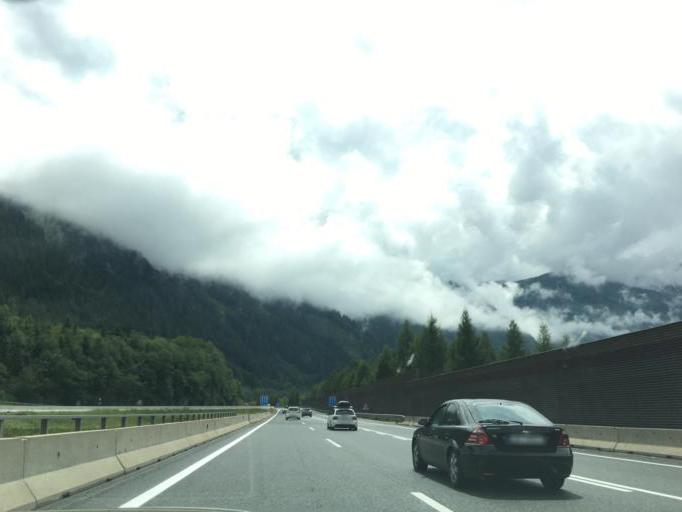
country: AT
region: Salzburg
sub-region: Politischer Bezirk Tamsweg
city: Sankt Michael im Lungau
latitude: 47.0909
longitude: 13.6084
